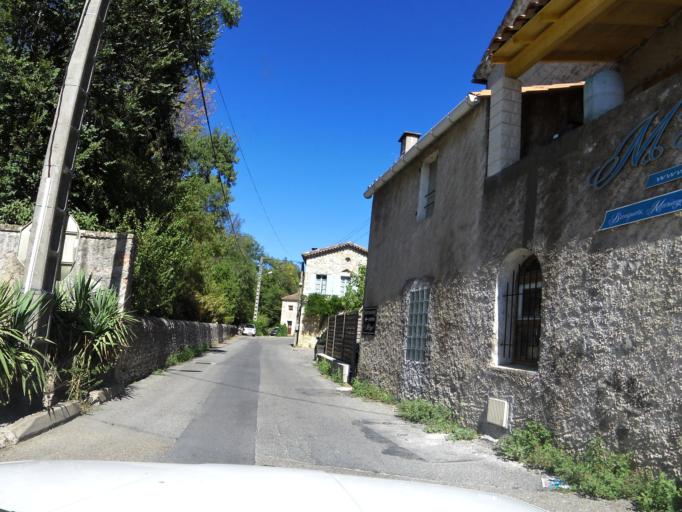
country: FR
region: Languedoc-Roussillon
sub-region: Departement du Gard
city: Vezenobres
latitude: 44.0478
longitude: 4.1434
